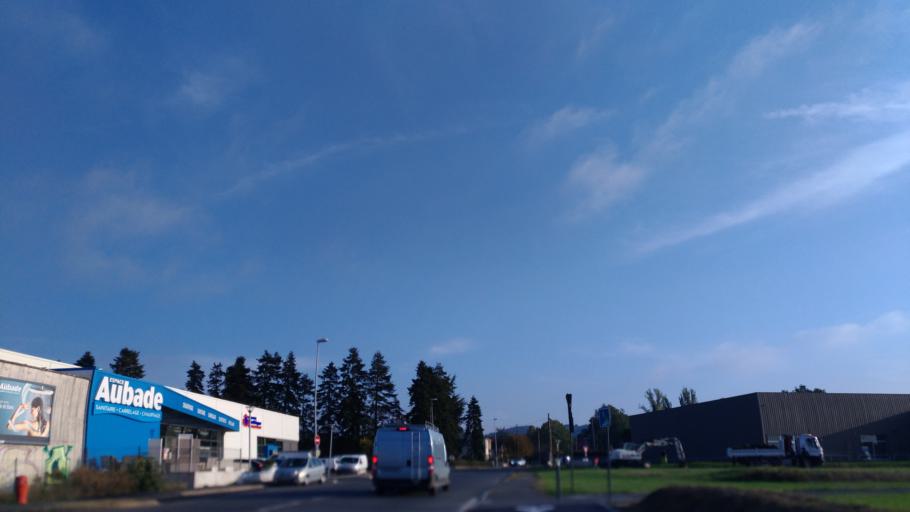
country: FR
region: Midi-Pyrenees
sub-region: Departement du Tarn
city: Puygouzon
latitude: 43.9178
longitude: 2.1666
